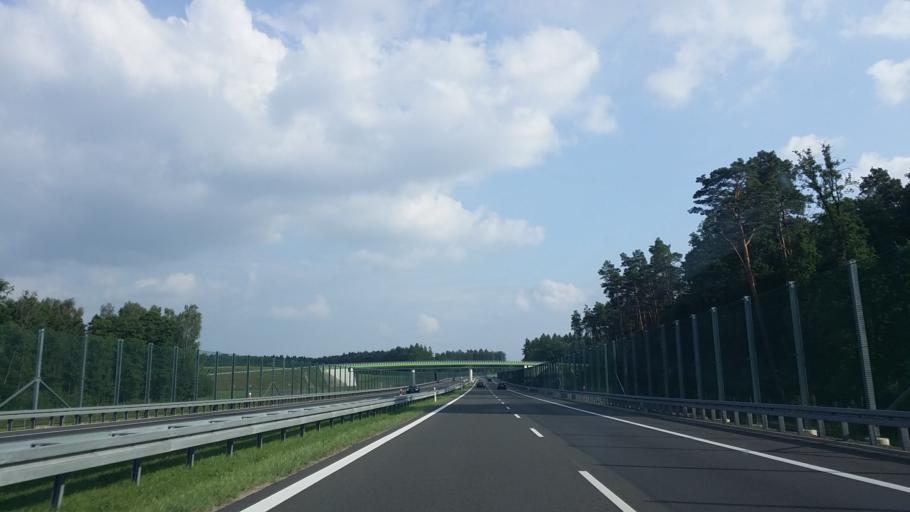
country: PL
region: Lubusz
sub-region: Powiat miedzyrzecki
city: Miedzyrzecz
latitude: 52.5123
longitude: 15.5500
